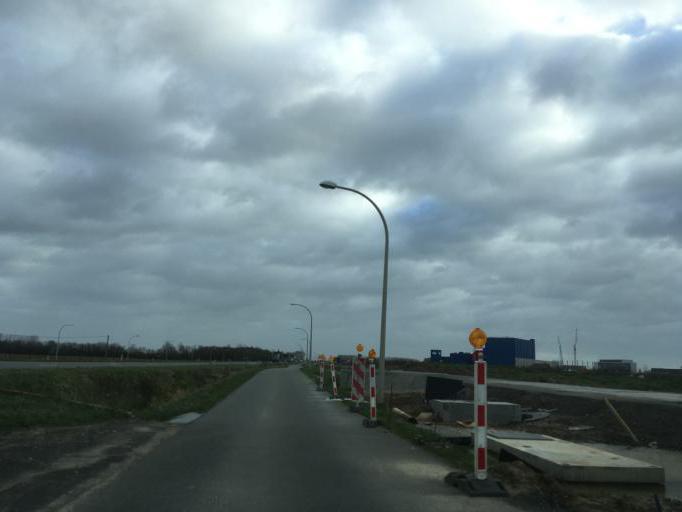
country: BE
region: Flanders
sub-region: Provincie West-Vlaanderen
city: Ardooie
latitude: 50.9784
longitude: 3.1538
